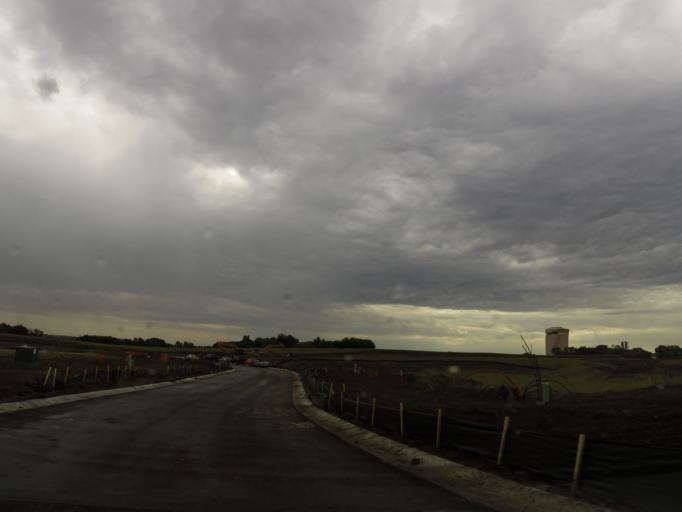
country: US
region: Minnesota
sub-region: Washington County
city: Lake Elmo
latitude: 44.9544
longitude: -92.9113
